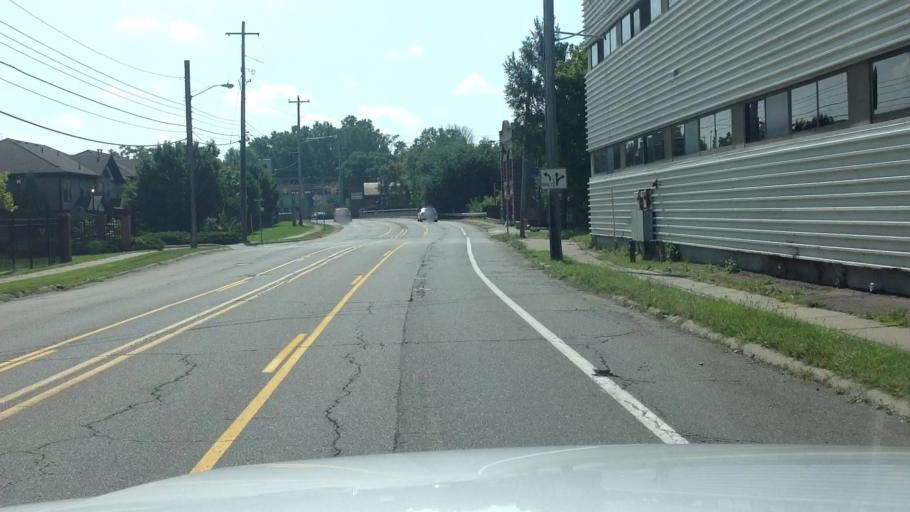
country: US
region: Michigan
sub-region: Genesee County
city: Flint
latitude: 43.0164
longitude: -83.6976
